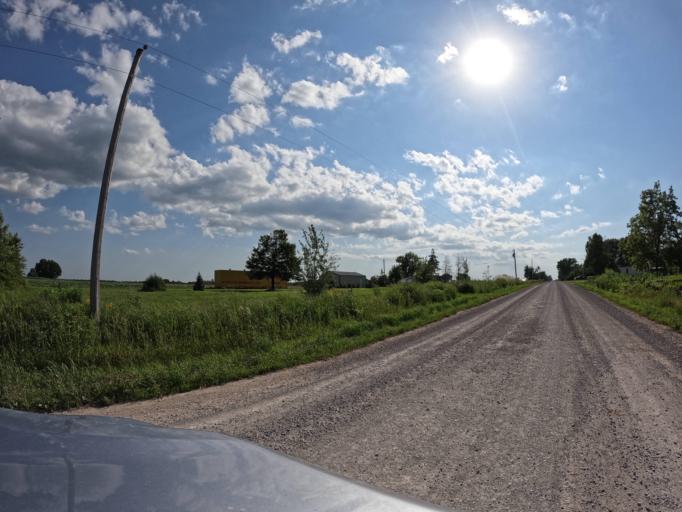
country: US
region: Iowa
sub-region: Appanoose County
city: Centerville
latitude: 40.7178
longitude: -93.0311
